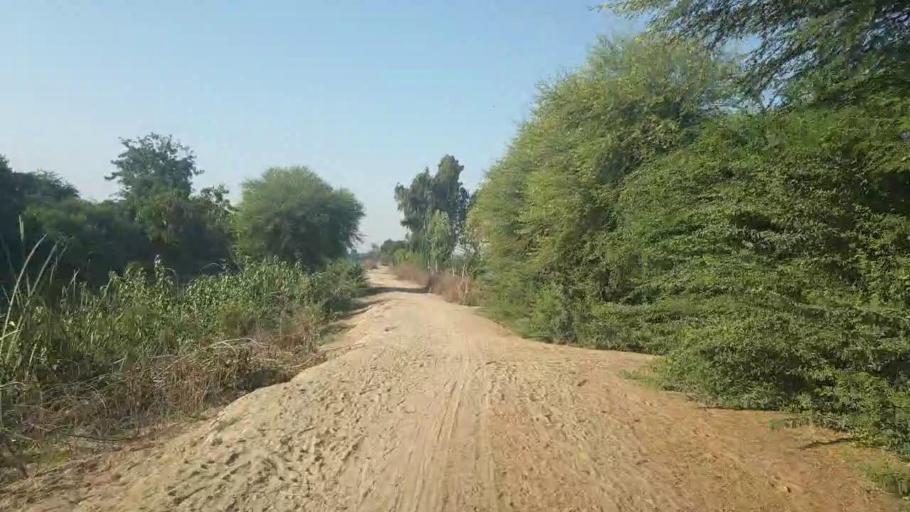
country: PK
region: Sindh
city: Tando Bago
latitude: 24.7174
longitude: 68.9138
